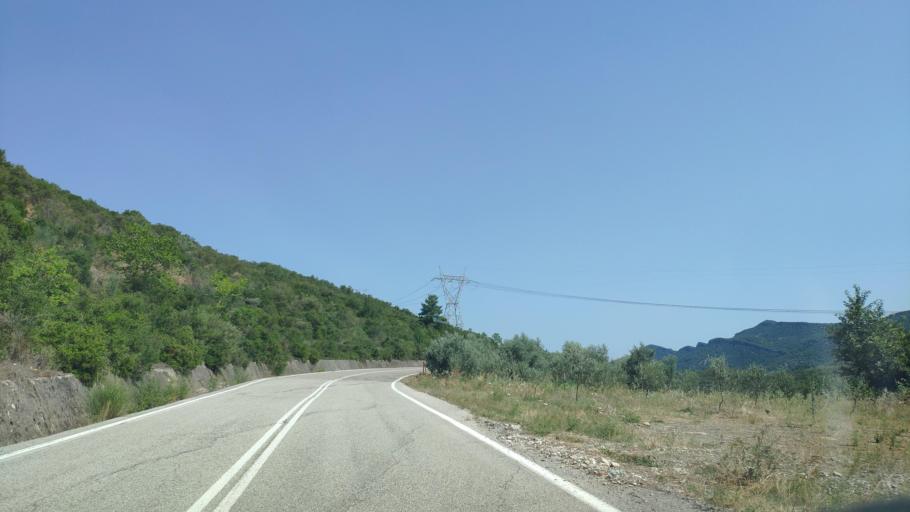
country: GR
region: West Greece
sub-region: Nomos Aitolias kai Akarnanias
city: Lepenou
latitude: 38.7520
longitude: 21.3416
